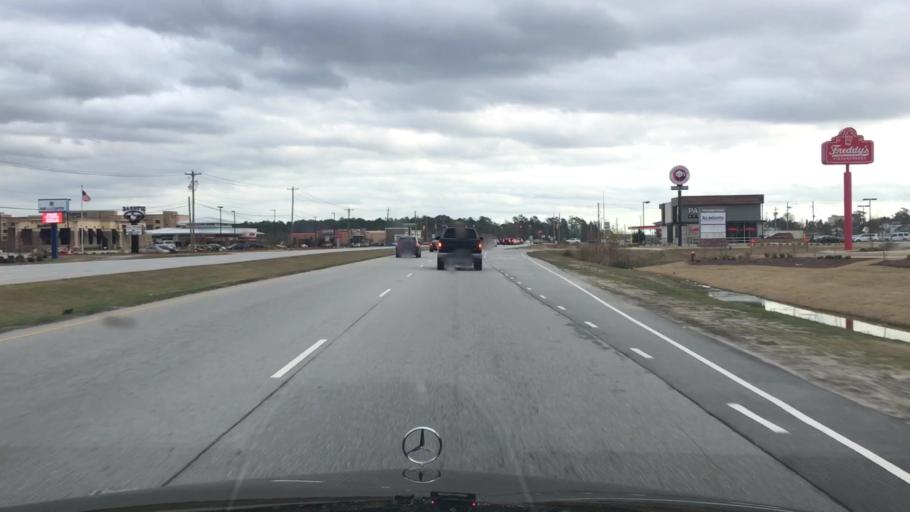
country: US
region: North Carolina
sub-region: Onslow County
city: Pumpkin Center
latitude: 34.7982
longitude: -77.4137
